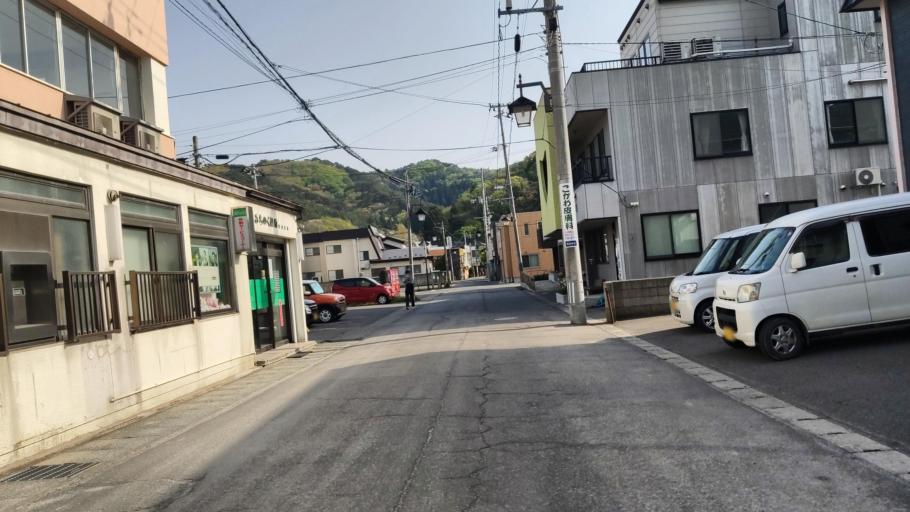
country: JP
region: Aomori
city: Aomori Shi
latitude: 40.8898
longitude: 140.8631
